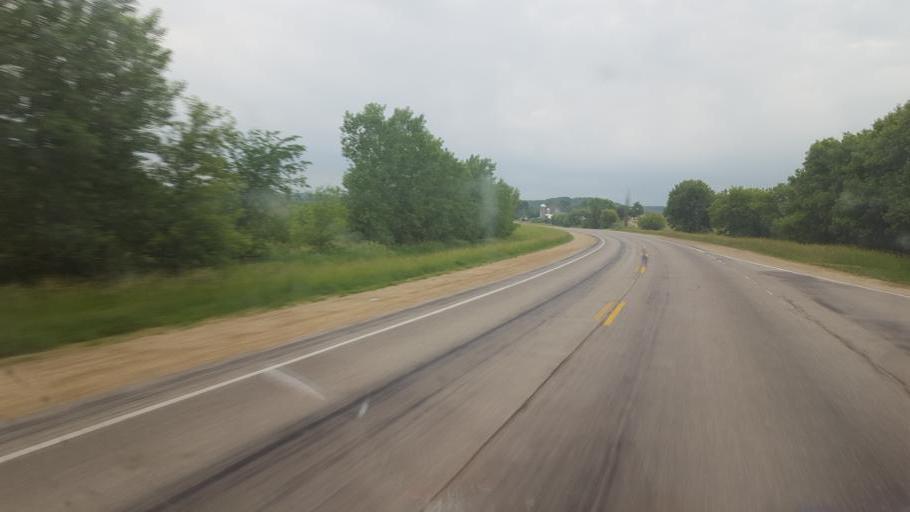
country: US
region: Wisconsin
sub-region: Vernon County
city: Hillsboro
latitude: 43.6574
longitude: -90.3676
